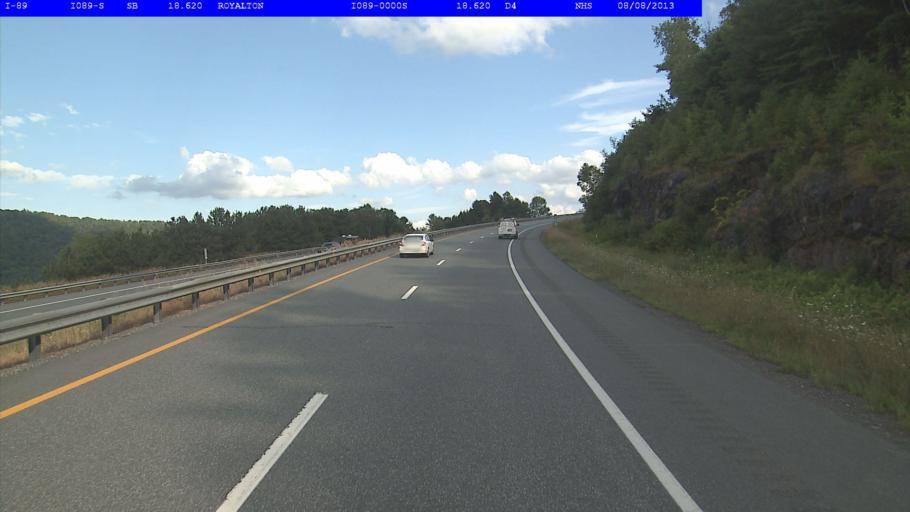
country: US
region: Vermont
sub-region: Orange County
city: Randolph
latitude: 43.8218
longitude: -72.5288
